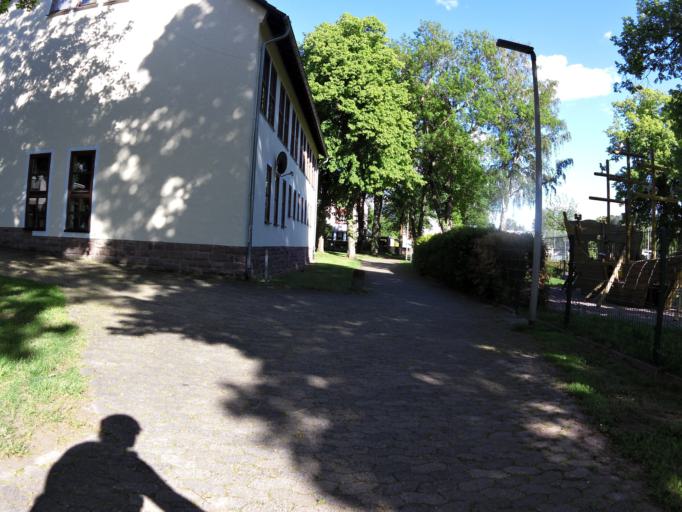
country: DE
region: Hesse
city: Philippsthal
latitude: 50.8419
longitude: 9.9988
